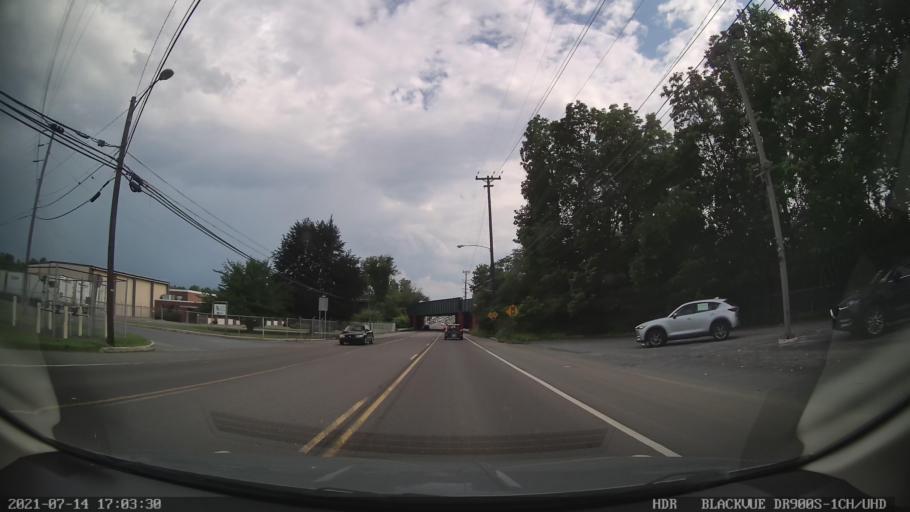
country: US
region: Pennsylvania
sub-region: Berks County
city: Muhlenberg Park
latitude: 40.3921
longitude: -75.9352
